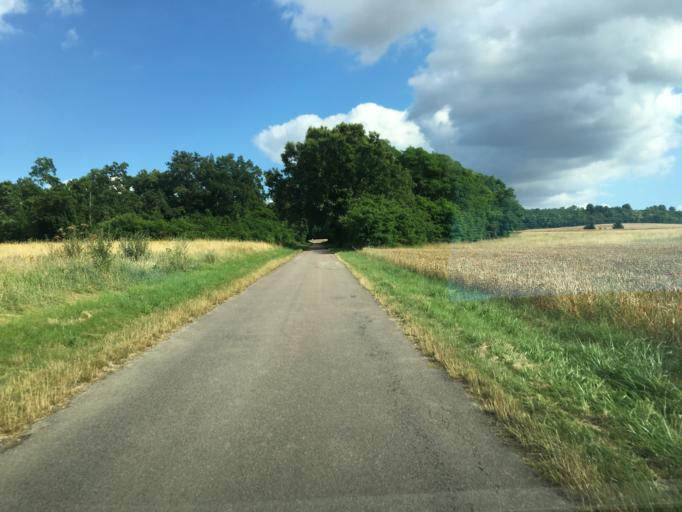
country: FR
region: Bourgogne
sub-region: Departement de l'Yonne
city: Aillant-sur-Tholon
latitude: 47.8267
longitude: 3.3760
